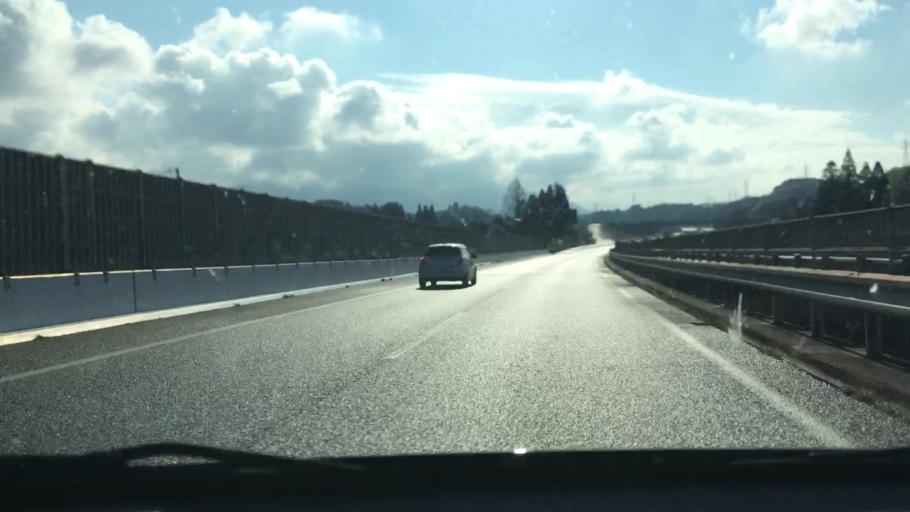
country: JP
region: Kumamoto
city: Matsubase
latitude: 32.5808
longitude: 130.7143
